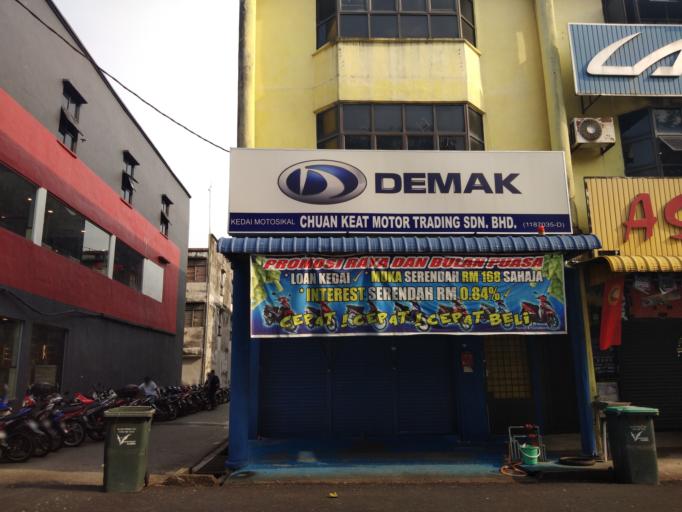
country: MY
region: Kedah
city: Kulim
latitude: 5.3774
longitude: 100.5409
